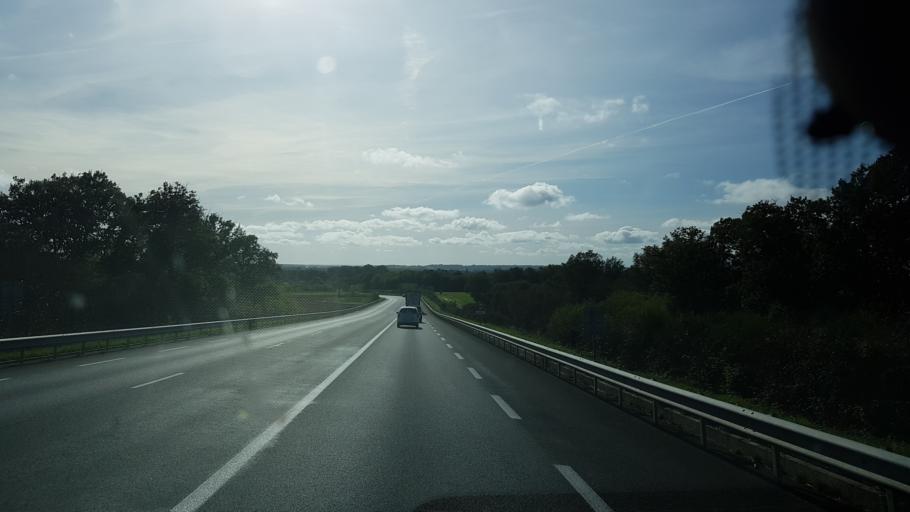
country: FR
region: Poitou-Charentes
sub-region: Departement de la Charente
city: Saint-Claud
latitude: 45.9031
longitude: 0.4829
